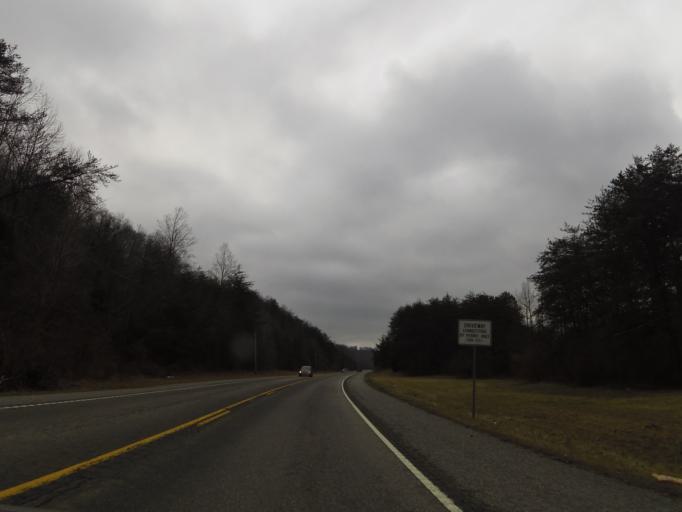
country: US
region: Tennessee
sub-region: Campbell County
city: Caryville
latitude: 36.4016
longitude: -84.2847
